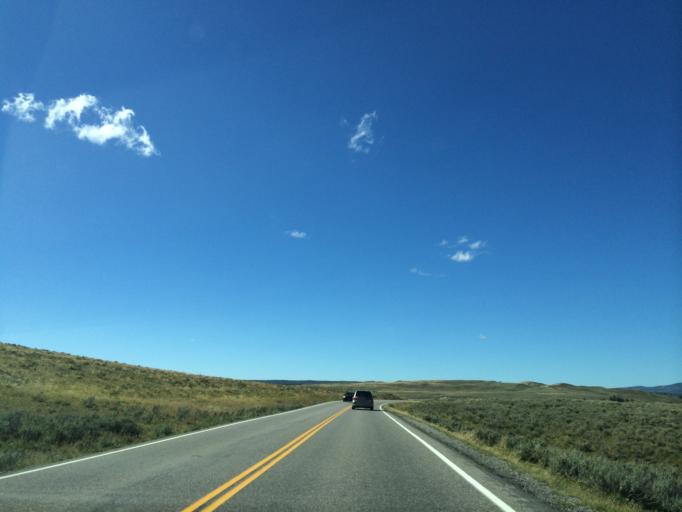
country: US
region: Montana
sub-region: Gallatin County
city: West Yellowstone
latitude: 44.6351
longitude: -110.4489
